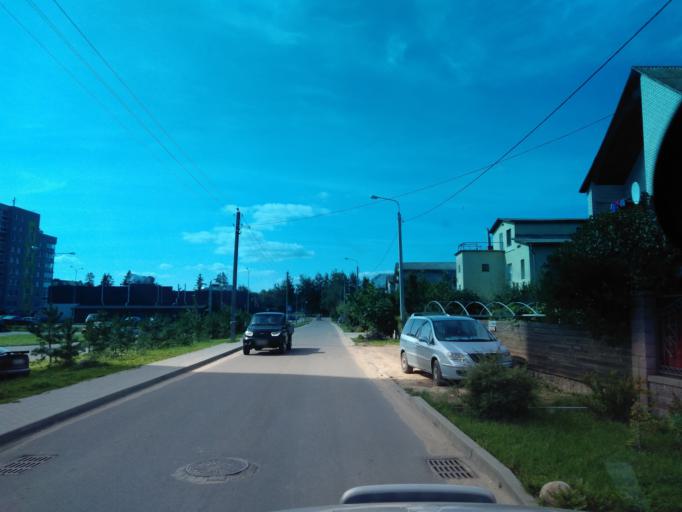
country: BY
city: Fanipol
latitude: 53.7530
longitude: 27.3362
